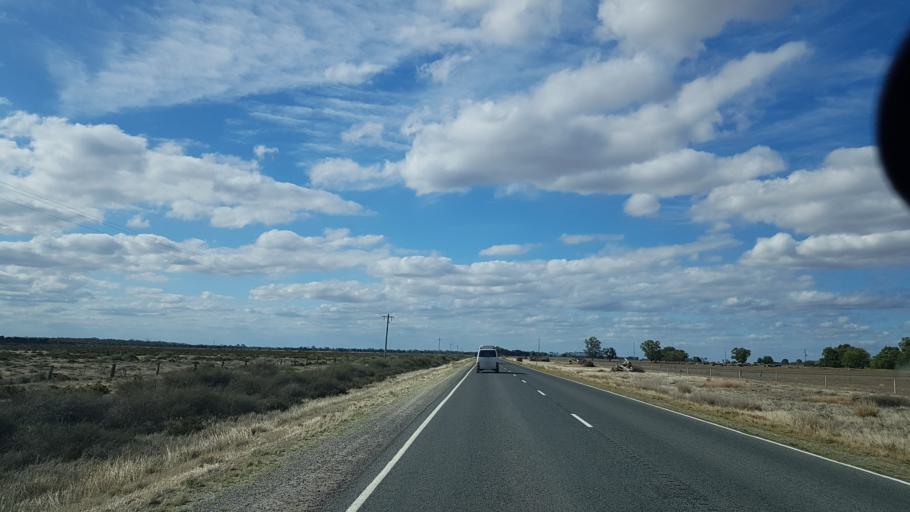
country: AU
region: Victoria
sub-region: Swan Hill
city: Swan Hill
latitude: -35.8382
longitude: 143.9408
